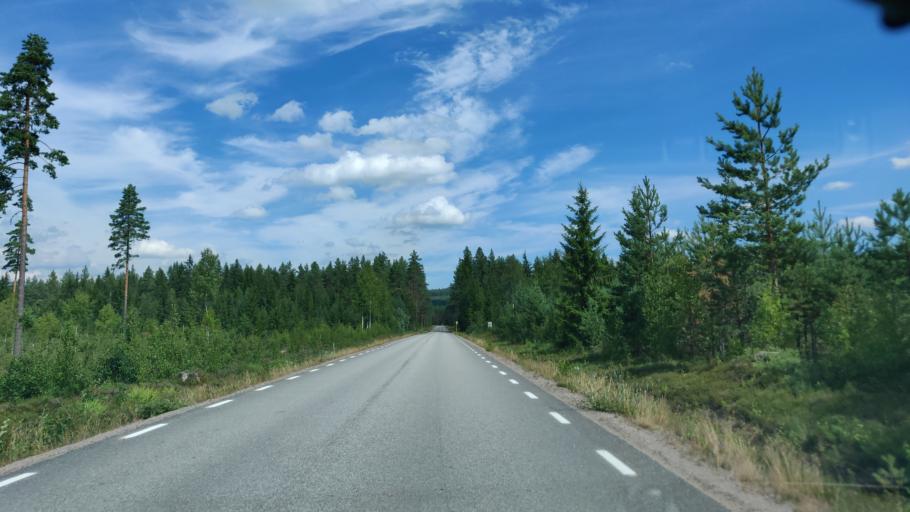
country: SE
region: Vaermland
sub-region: Hagfors Kommun
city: Ekshaerad
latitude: 60.0800
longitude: 13.4993
